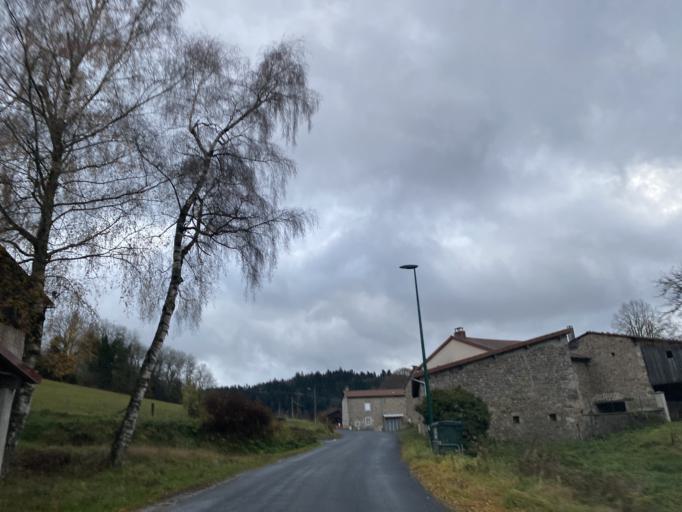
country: FR
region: Auvergne
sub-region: Departement du Puy-de-Dome
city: Cunlhat
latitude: 45.5909
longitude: 3.5603
